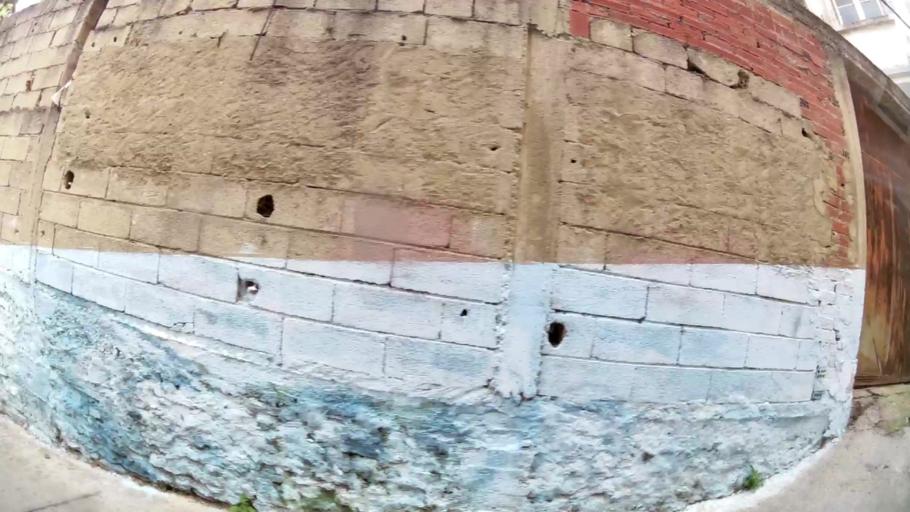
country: MA
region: Tanger-Tetouan
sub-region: Tanger-Assilah
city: Tangier
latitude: 35.7678
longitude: -5.7904
